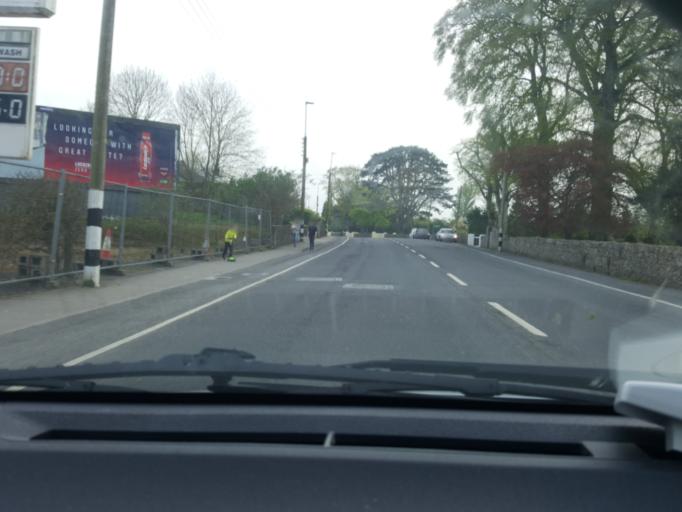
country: IE
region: Munster
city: Cahir
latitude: 52.3814
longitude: -7.9203
